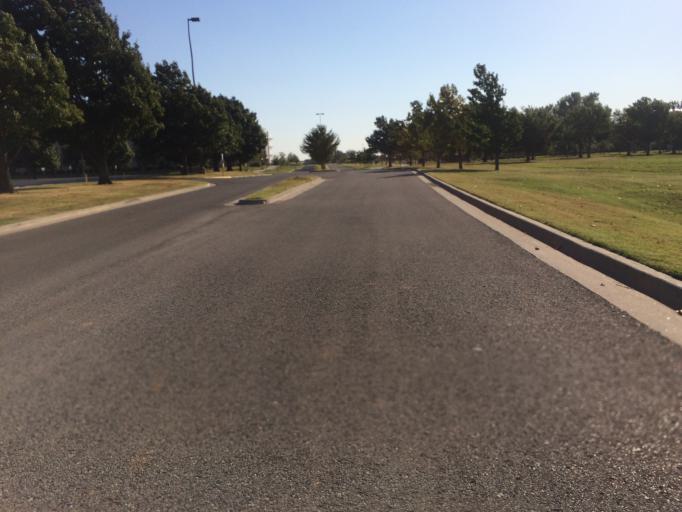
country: US
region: Oklahoma
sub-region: Cleveland County
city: Norman
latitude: 35.1852
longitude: -97.4429
